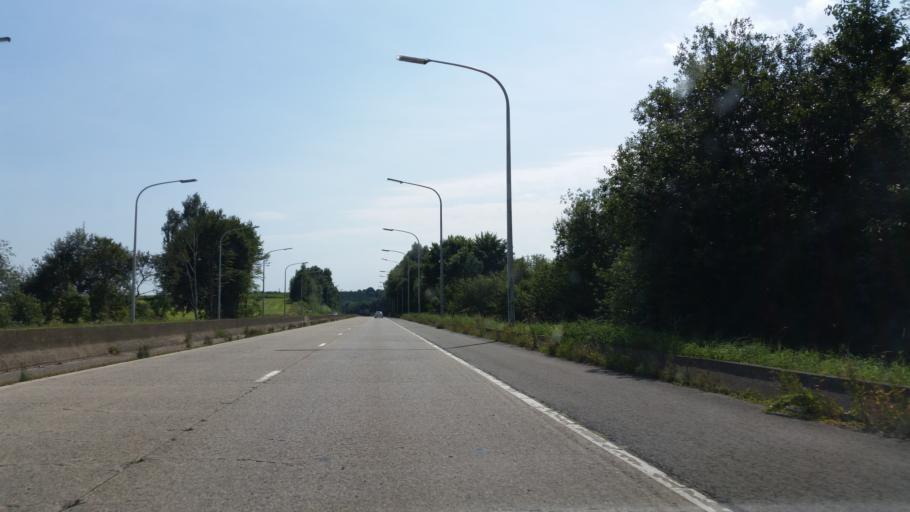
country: BE
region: Wallonia
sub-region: Province de Namur
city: Hamois
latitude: 50.2947
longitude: 5.1730
